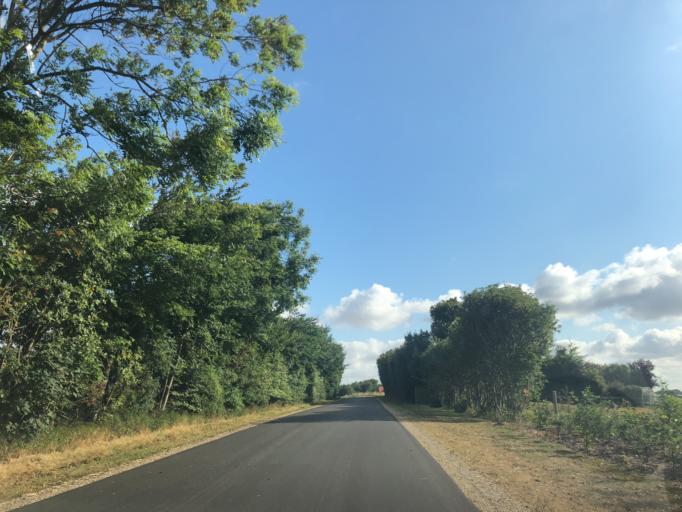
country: DK
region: Central Jutland
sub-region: Holstebro Kommune
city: Vinderup
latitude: 56.6173
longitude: 8.8702
